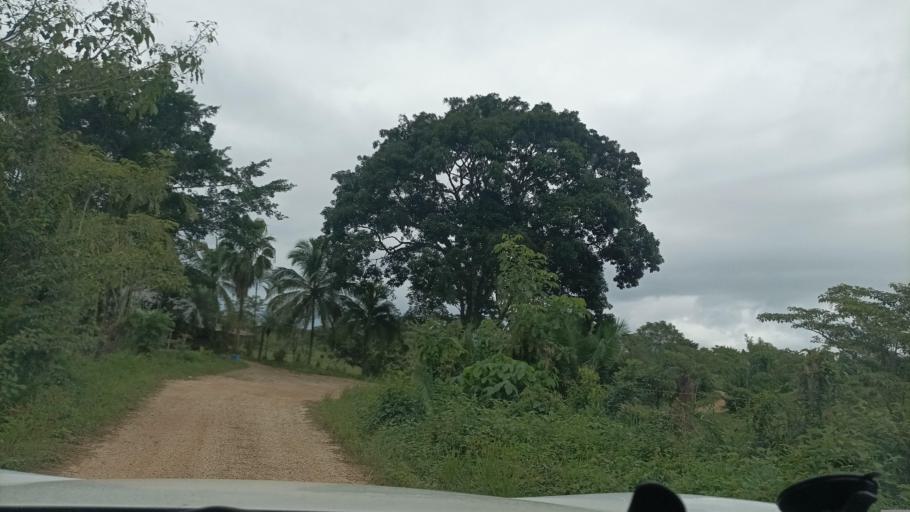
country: MX
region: Veracruz
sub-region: Uxpanapa
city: Poblado Cinco
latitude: 17.4903
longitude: -94.5713
